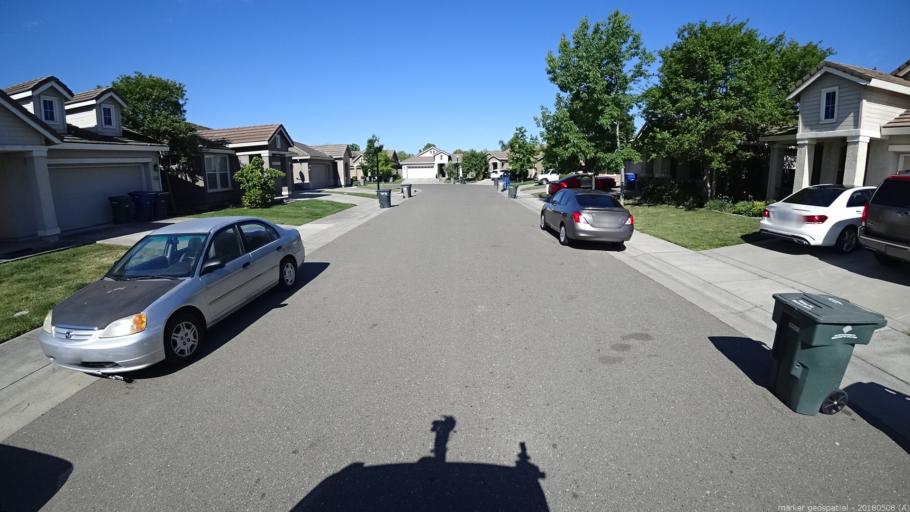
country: US
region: California
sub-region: Sacramento County
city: Elverta
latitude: 38.6841
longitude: -121.4992
